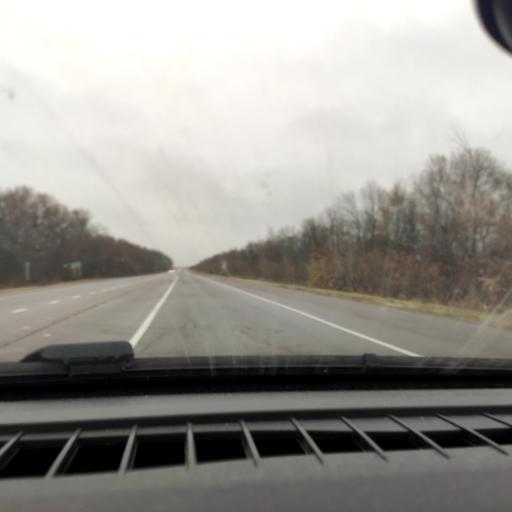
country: RU
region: Voronezj
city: Kolodeznyy
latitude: 51.2943
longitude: 39.0400
